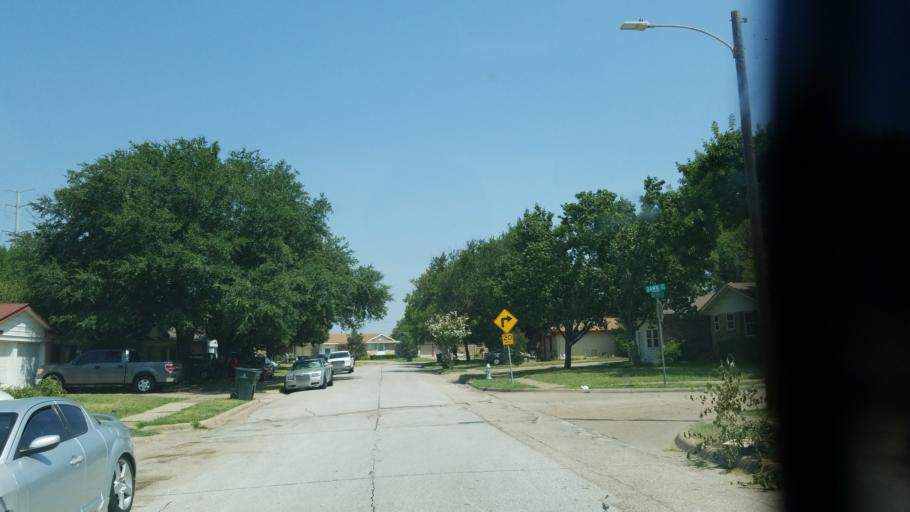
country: US
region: Texas
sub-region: Dallas County
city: Garland
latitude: 32.9295
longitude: -96.6254
